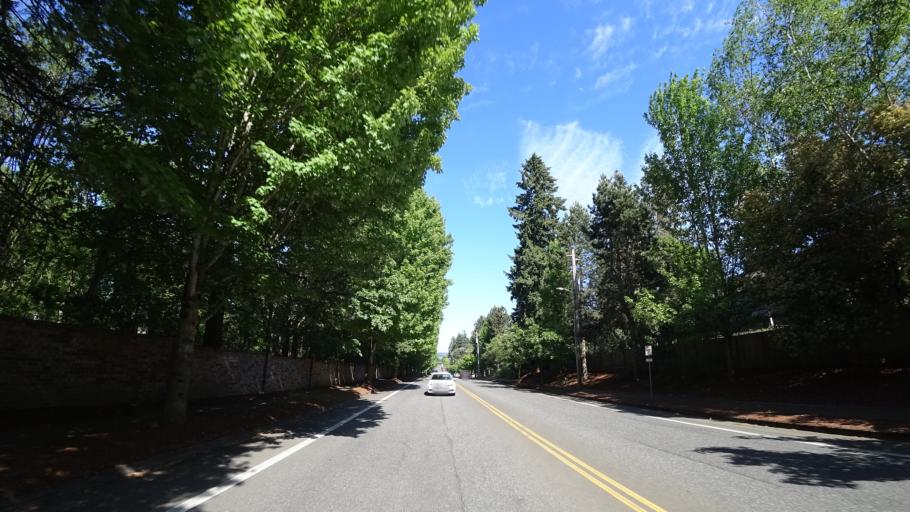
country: US
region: Oregon
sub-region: Washington County
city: Beaverton
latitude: 45.4548
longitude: -122.8123
